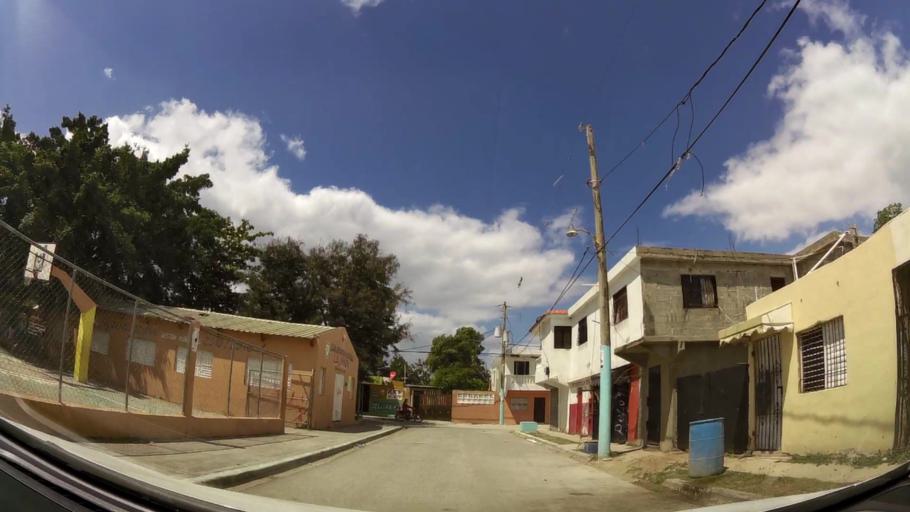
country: DO
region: Santo Domingo
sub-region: Santo Domingo
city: Boca Chica
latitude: 18.4500
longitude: -69.6545
